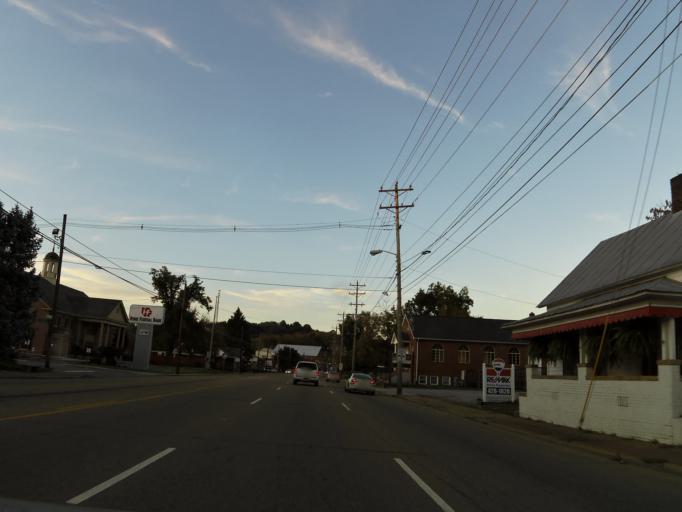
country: US
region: Tennessee
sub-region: Sevier County
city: Sevierville
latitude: 35.8645
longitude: -83.5639
